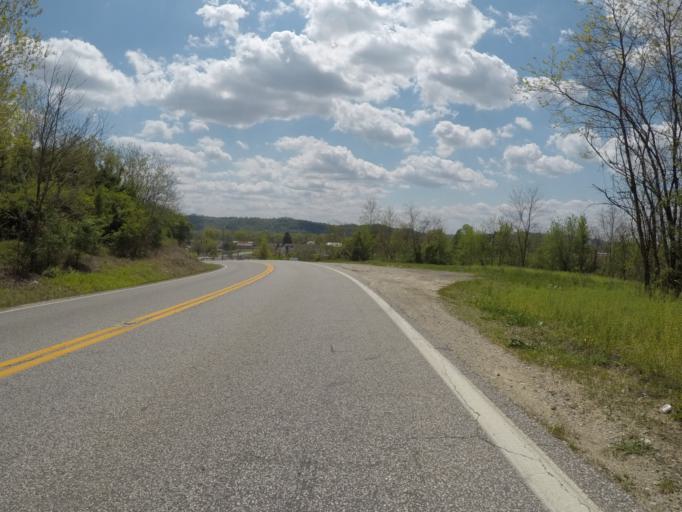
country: US
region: West Virginia
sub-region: Cabell County
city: Pea Ridge
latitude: 38.4498
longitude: -82.3768
